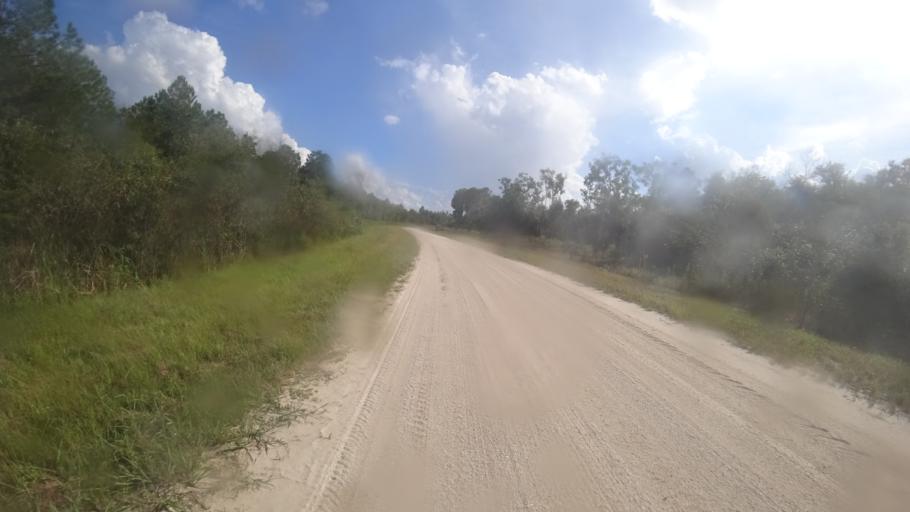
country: US
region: Florida
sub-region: Hillsborough County
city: Wimauma
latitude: 27.6062
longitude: -82.1194
